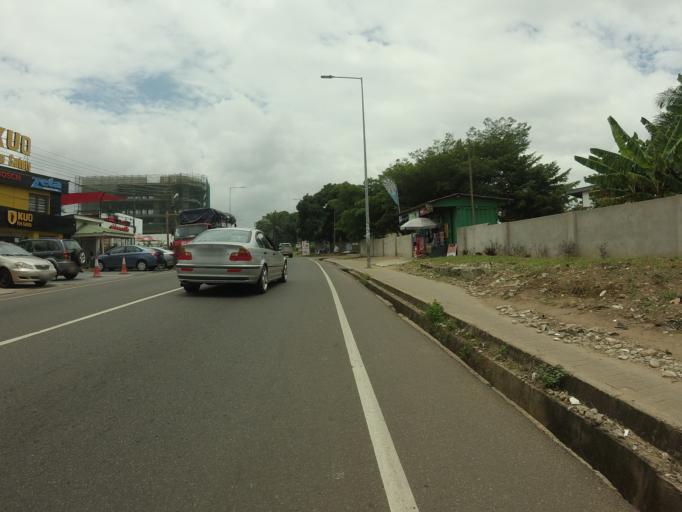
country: GH
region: Greater Accra
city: Accra
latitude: 5.5663
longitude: -0.1699
